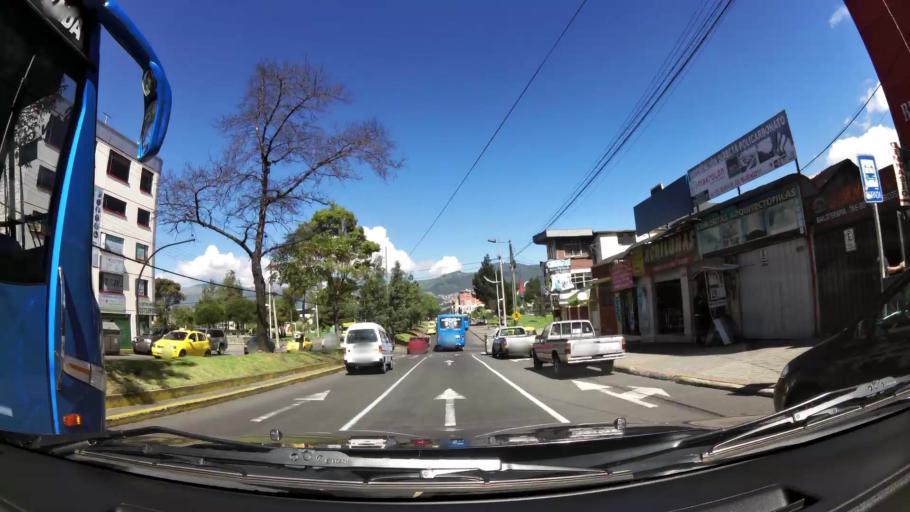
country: EC
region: Pichincha
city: Quito
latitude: -0.2467
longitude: -78.5229
